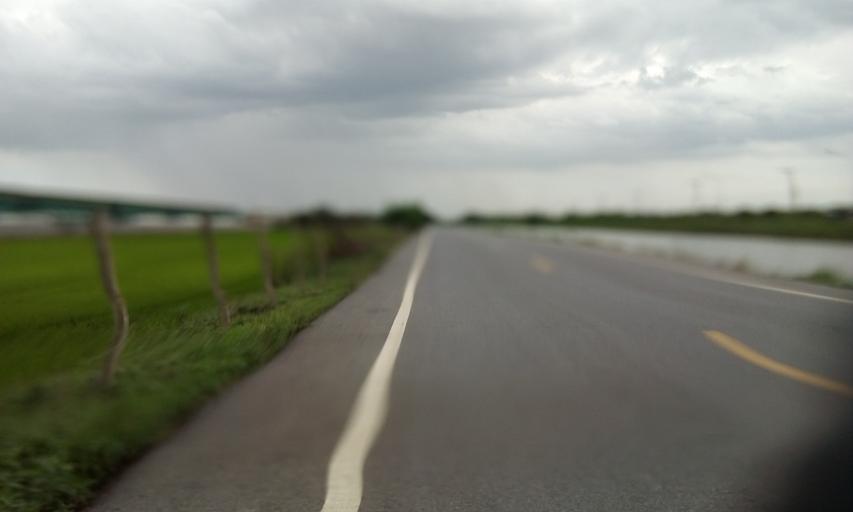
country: TH
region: Pathum Thani
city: Nong Suea
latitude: 14.0687
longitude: 100.8468
